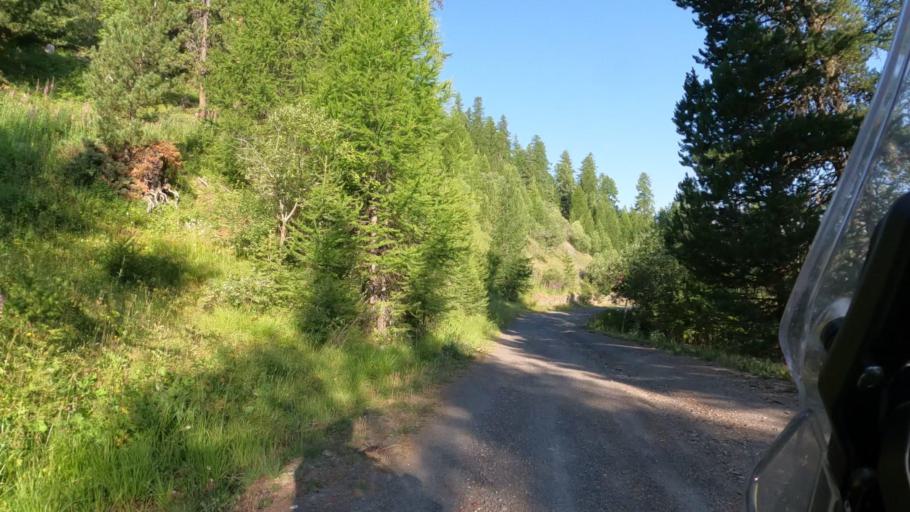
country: FR
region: Provence-Alpes-Cote d'Azur
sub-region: Departement des Hautes-Alpes
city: Guillestre
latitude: 44.6172
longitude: 6.6456
